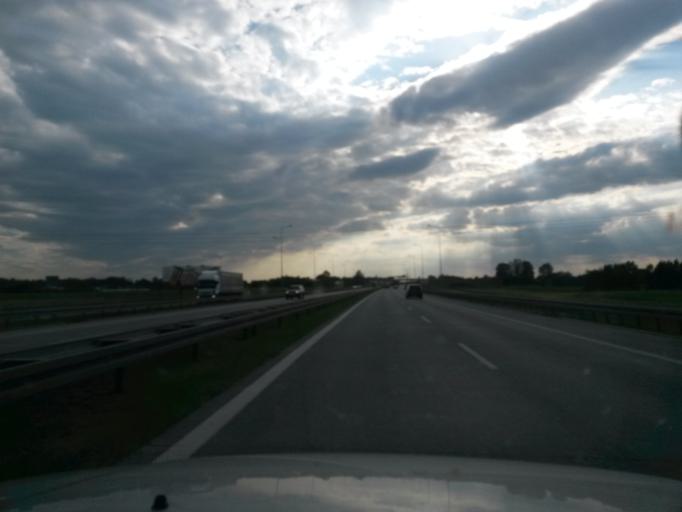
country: PL
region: Lodz Voivodeship
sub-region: Piotrkow Trybunalski
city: Piotrkow Trybunalski
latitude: 51.4422
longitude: 19.6796
